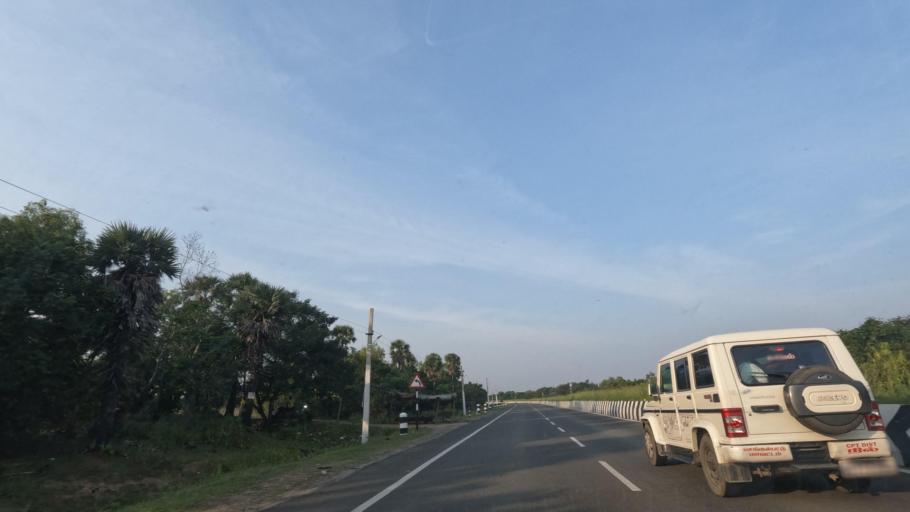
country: IN
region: Tamil Nadu
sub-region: Kancheepuram
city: Mamallapuram
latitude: 12.6697
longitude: 80.2106
